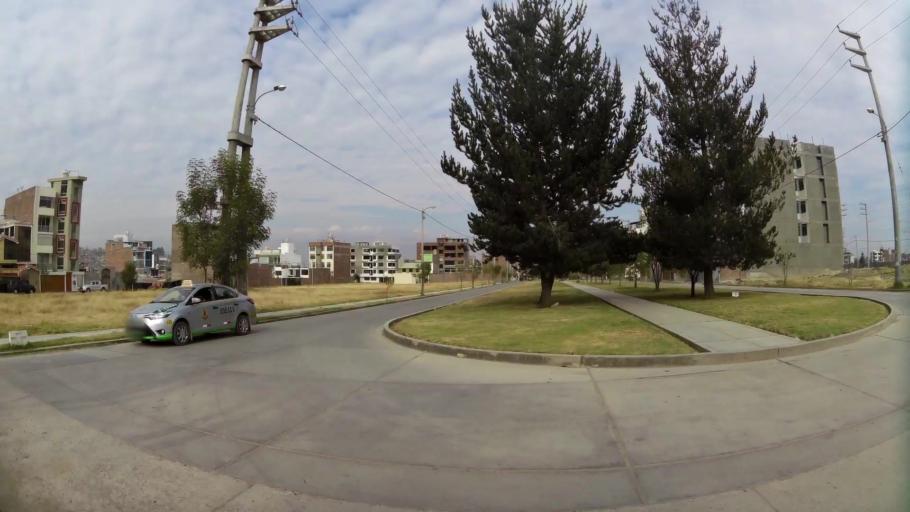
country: PE
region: Junin
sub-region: Provincia de Huancayo
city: Huancayo
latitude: -12.0483
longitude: -75.1893
